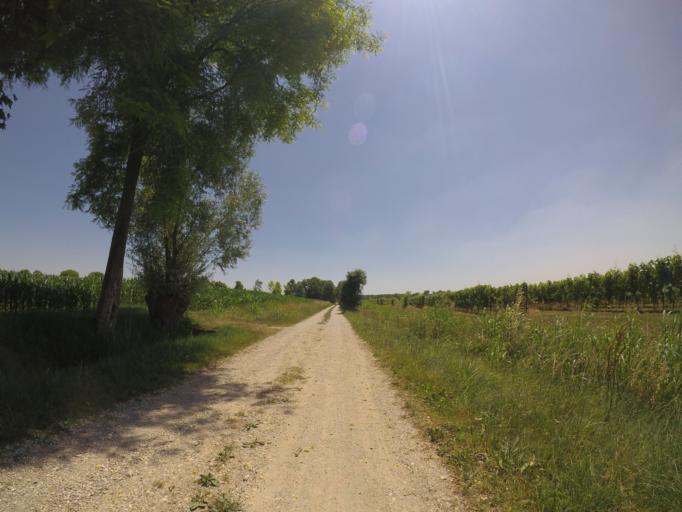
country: IT
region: Friuli Venezia Giulia
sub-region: Provincia di Udine
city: Bertiolo
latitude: 45.9423
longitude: 13.0163
